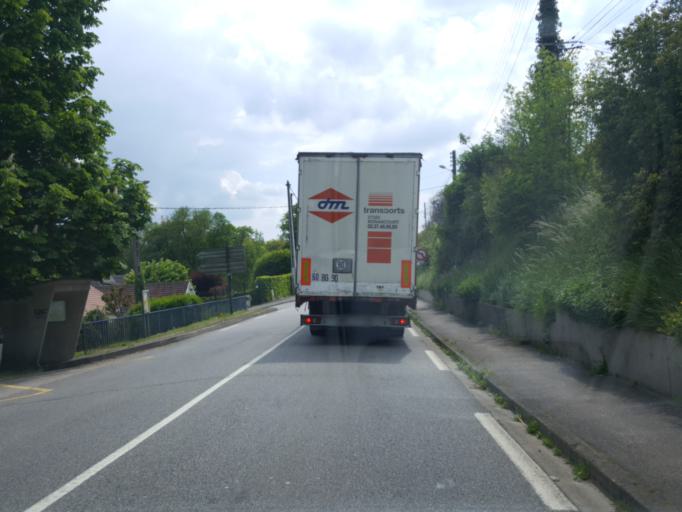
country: FR
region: Ile-de-France
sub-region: Departement des Yvelines
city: Mantes-la-Ville
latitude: 48.9506
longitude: 1.6991
